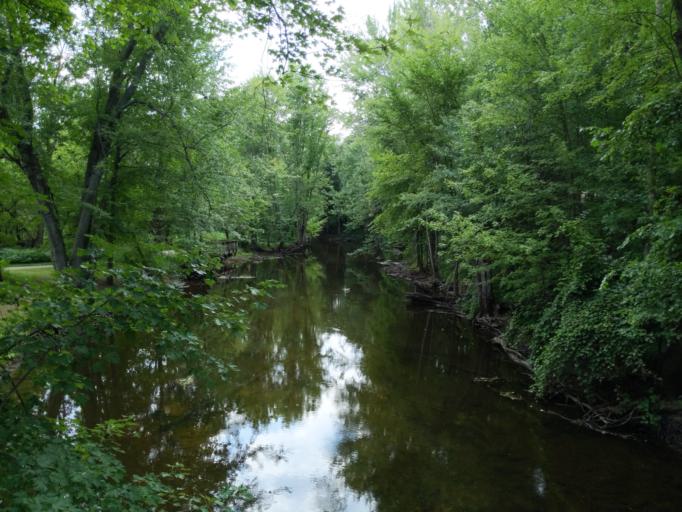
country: US
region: Michigan
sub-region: Clinton County
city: DeWitt
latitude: 42.8403
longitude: -84.5653
